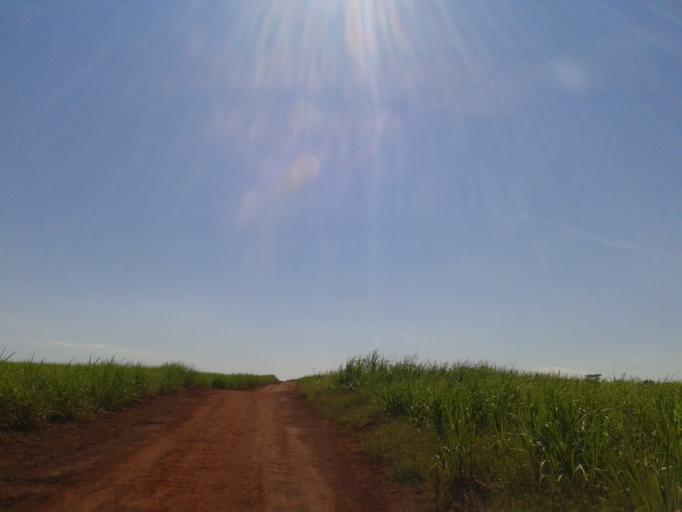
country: BR
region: Minas Gerais
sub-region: Centralina
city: Centralina
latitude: -18.6207
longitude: -49.2752
